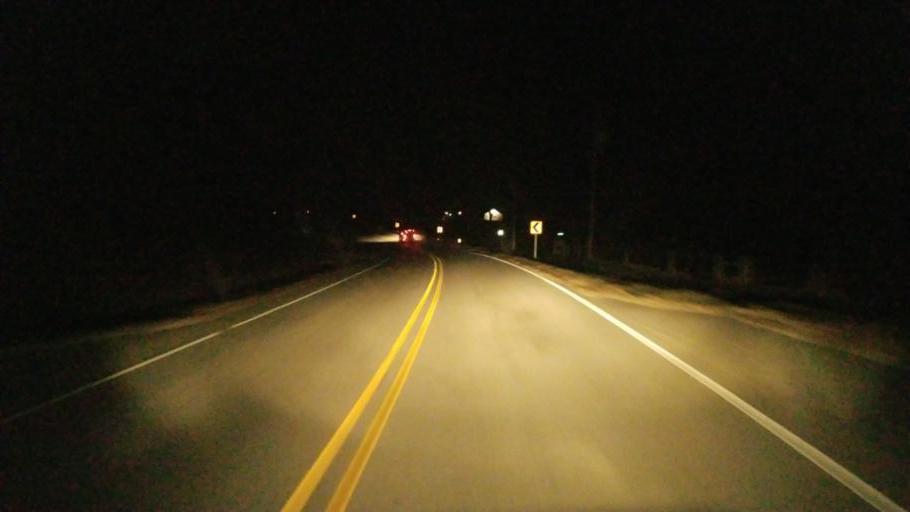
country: US
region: Illinois
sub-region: Henderson County
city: Oquawka
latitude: 40.7754
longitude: -90.8648
